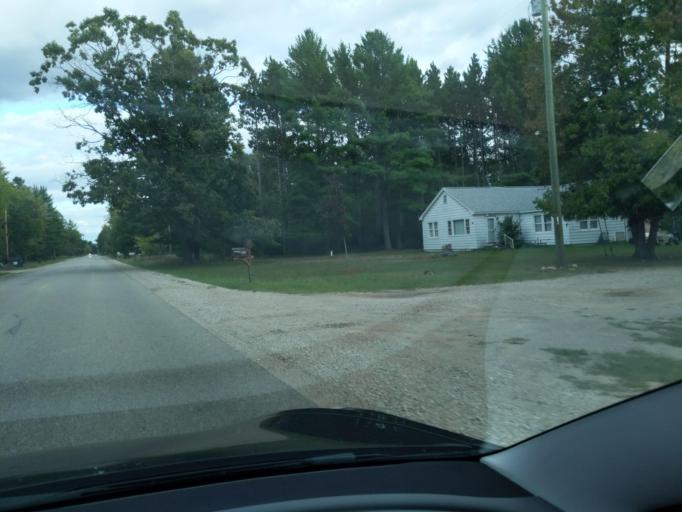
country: US
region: Michigan
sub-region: Kalkaska County
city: Rapid City
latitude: 44.8418
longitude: -85.3019
